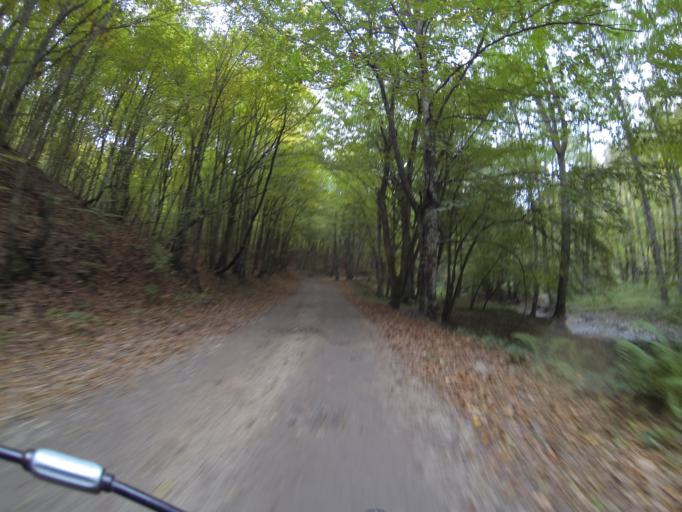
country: RO
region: Gorj
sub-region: Comuna Tismana
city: Sohodol
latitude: 45.0578
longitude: 22.9013
